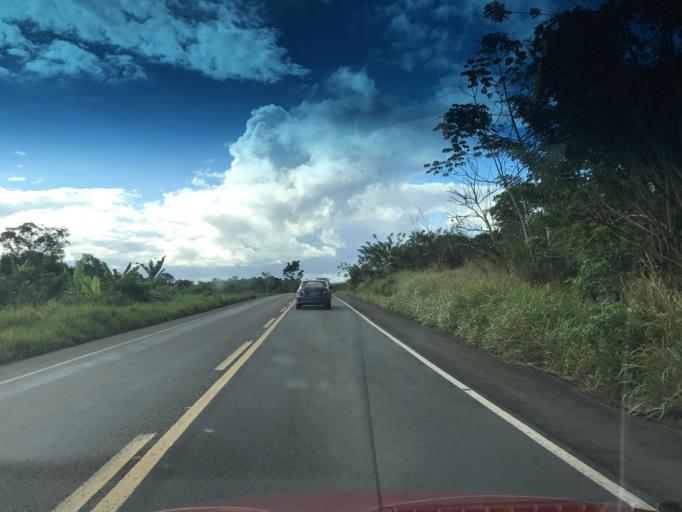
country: BR
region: Bahia
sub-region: Ibirapitanga
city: Ibirapitanga
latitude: -14.1649
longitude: -39.3286
